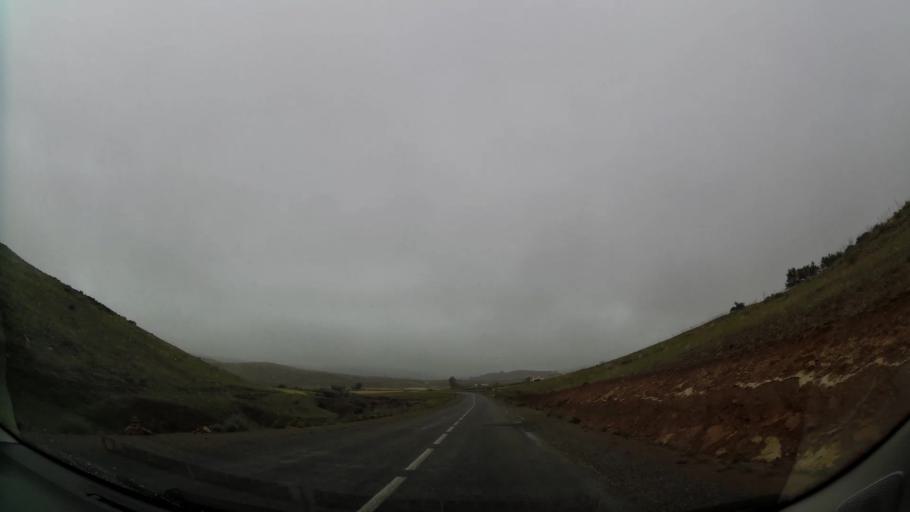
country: MA
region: Oriental
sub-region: Nador
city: Boudinar
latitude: 35.1091
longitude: -3.5697
